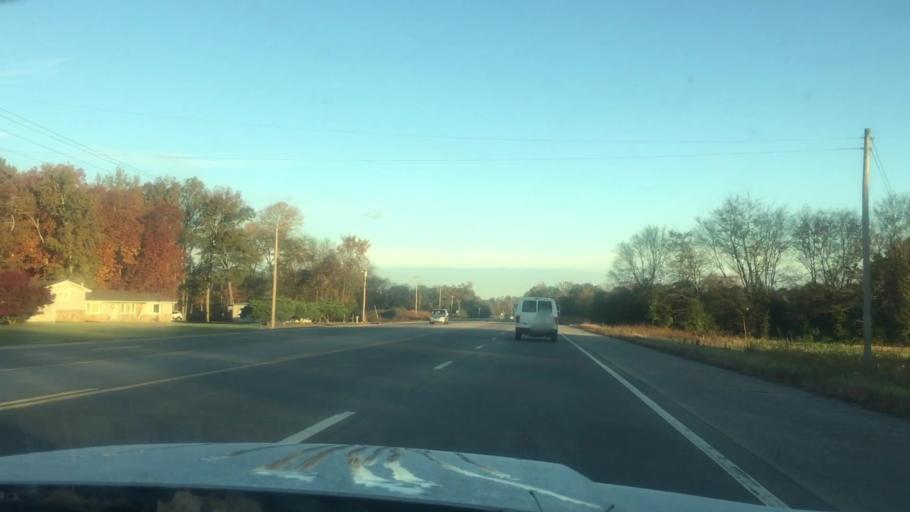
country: US
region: Tennessee
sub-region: Franklin County
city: Estill Springs
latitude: 35.2368
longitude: -86.1120
